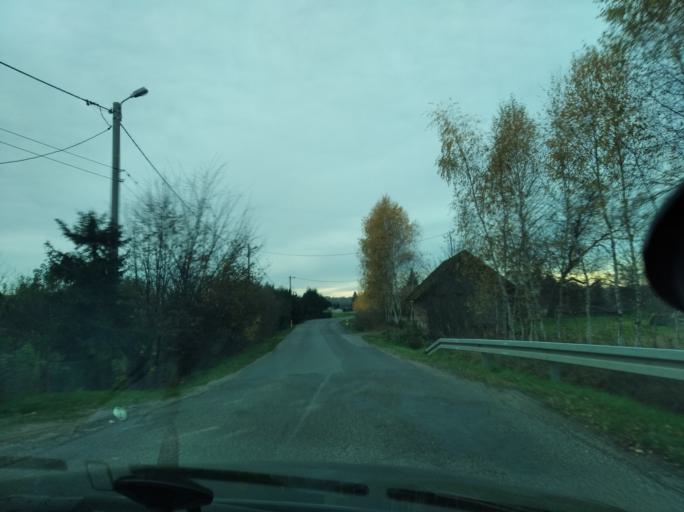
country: PL
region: Subcarpathian Voivodeship
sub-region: Powiat lancucki
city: Czarna
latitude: 50.0890
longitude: 22.1852
